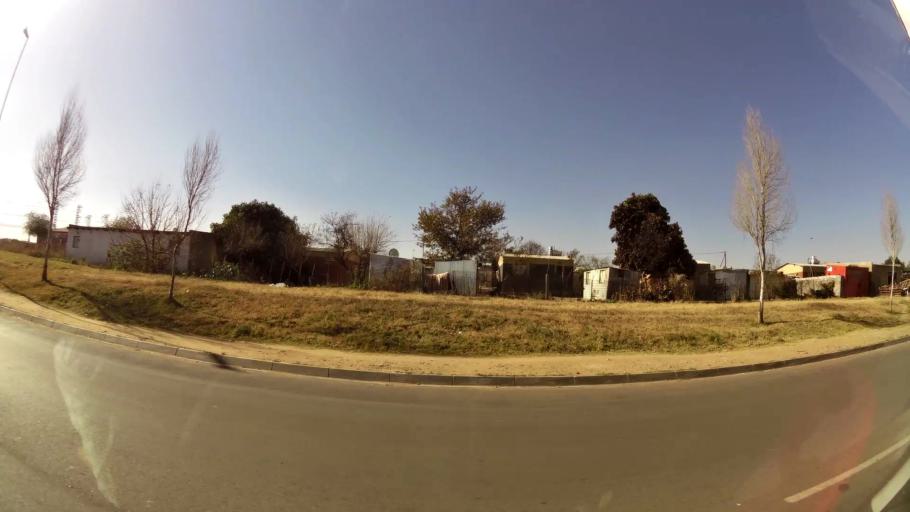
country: ZA
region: Gauteng
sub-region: Ekurhuleni Metropolitan Municipality
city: Tembisa
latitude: -26.0270
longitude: 28.2327
